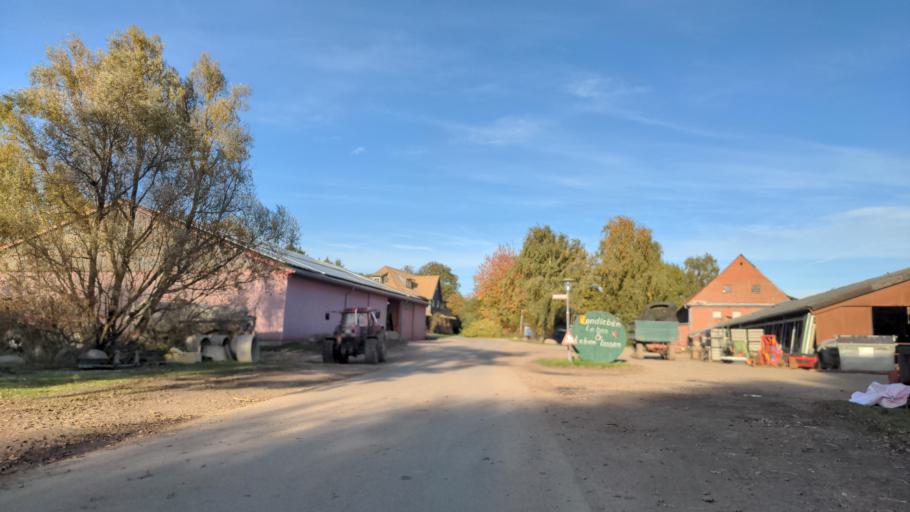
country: DE
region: Schleswig-Holstein
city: Kirchnuchel
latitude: 54.1966
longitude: 10.7005
